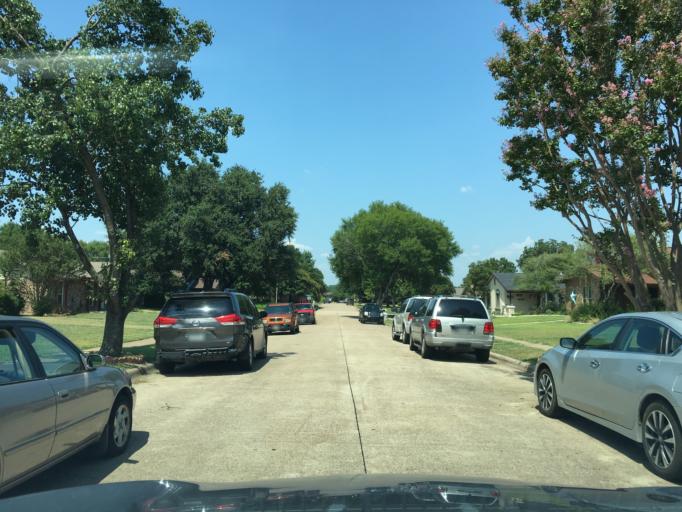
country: US
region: Texas
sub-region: Dallas County
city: Garland
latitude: 32.9649
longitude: -96.6673
